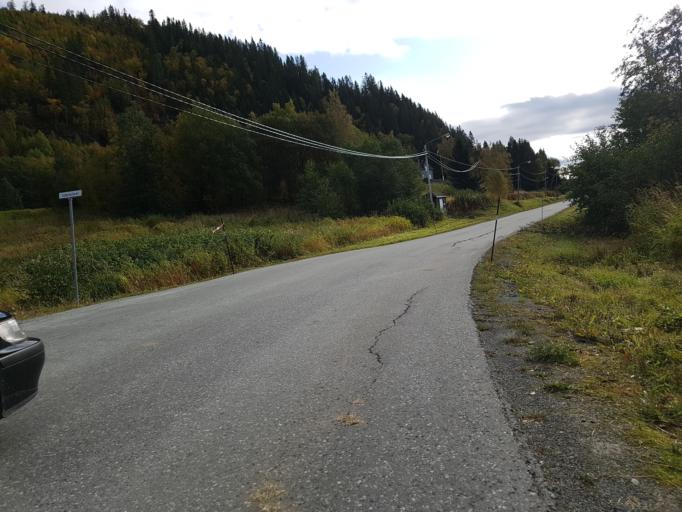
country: NO
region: Sor-Trondelag
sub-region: Klaebu
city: Klaebu
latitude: 63.3974
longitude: 10.5553
